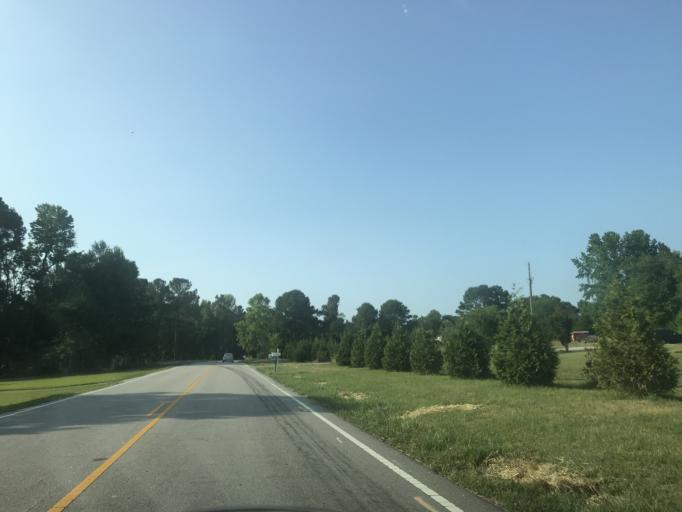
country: US
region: North Carolina
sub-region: Wake County
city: Knightdale
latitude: 35.8367
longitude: -78.5015
